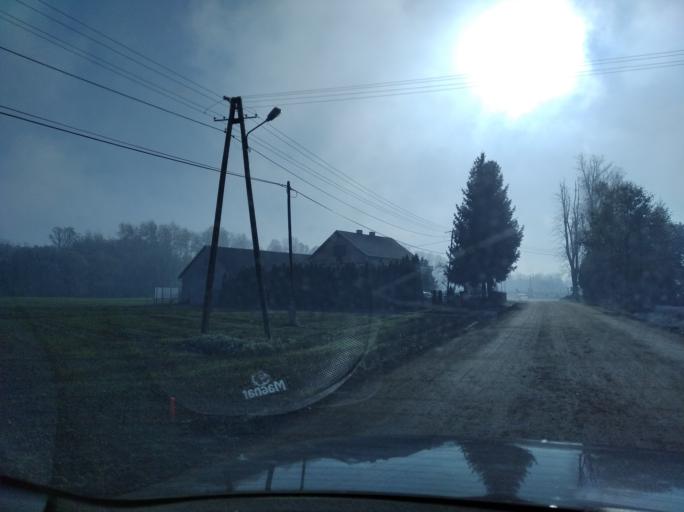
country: PL
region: Subcarpathian Voivodeship
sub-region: Powiat strzyzowski
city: Wysoka Strzyzowska
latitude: 49.8674
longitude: 21.7061
